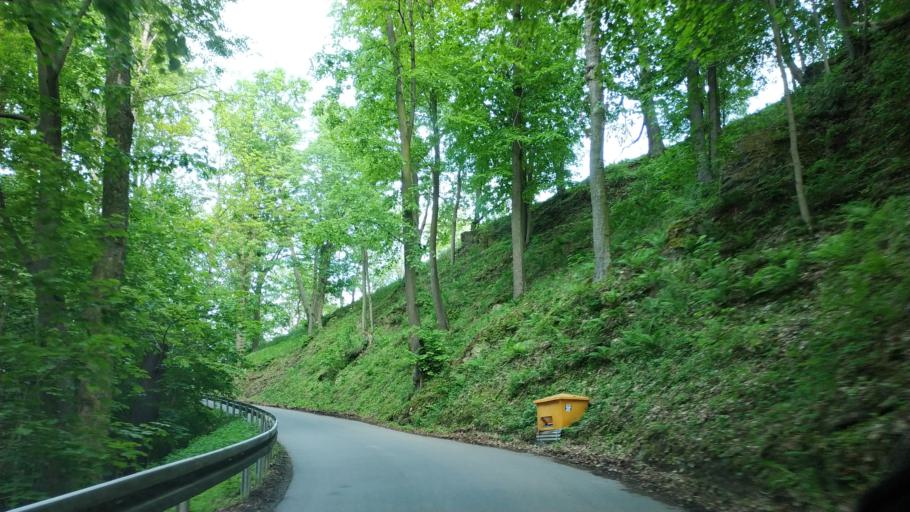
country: DE
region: Saxony
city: Pohl
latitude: 50.5553
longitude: 12.1619
